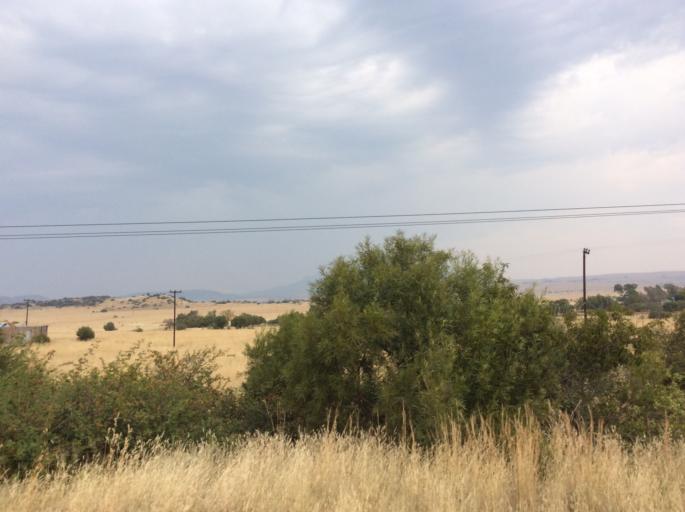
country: LS
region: Mafeteng
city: Mafeteng
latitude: -29.9871
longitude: 27.0215
